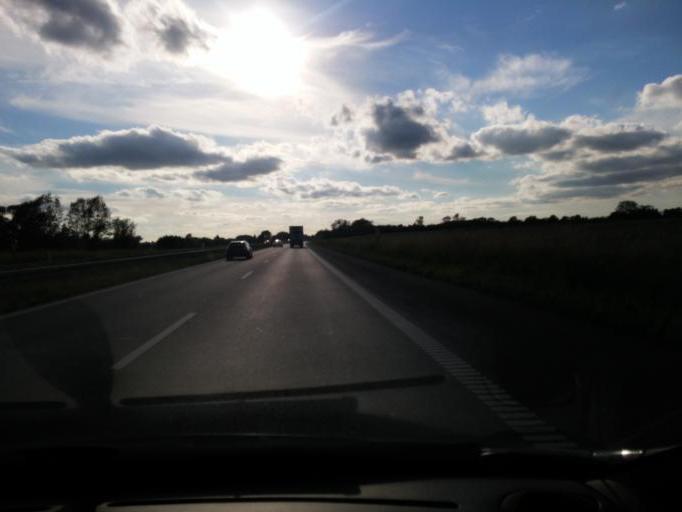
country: DK
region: South Denmark
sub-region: Nyborg Kommune
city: Ullerslev
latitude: 55.3353
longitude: 10.7114
